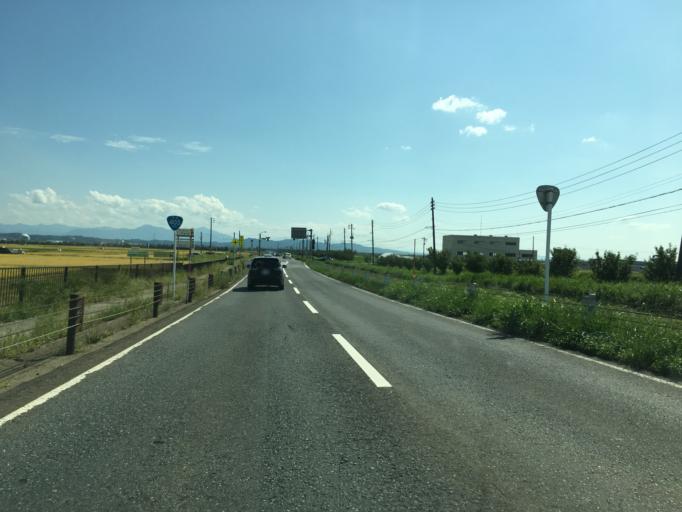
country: JP
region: Niigata
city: Kameda-honcho
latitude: 37.8335
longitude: 139.0967
